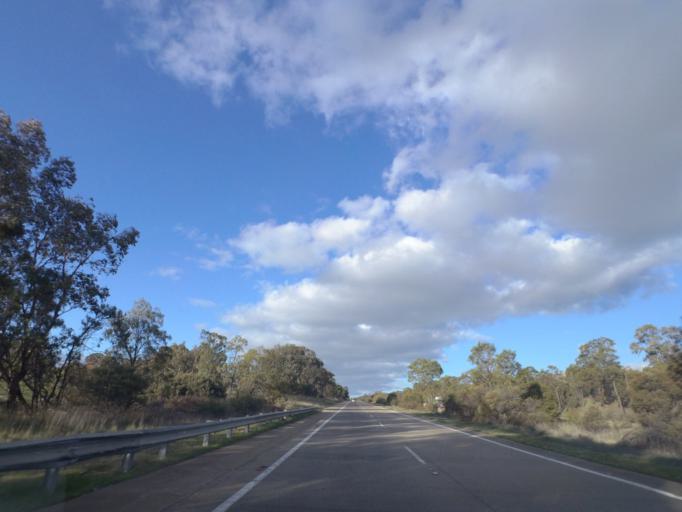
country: AU
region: New South Wales
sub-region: Yass Valley
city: Yass
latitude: -34.8055
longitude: 148.4757
